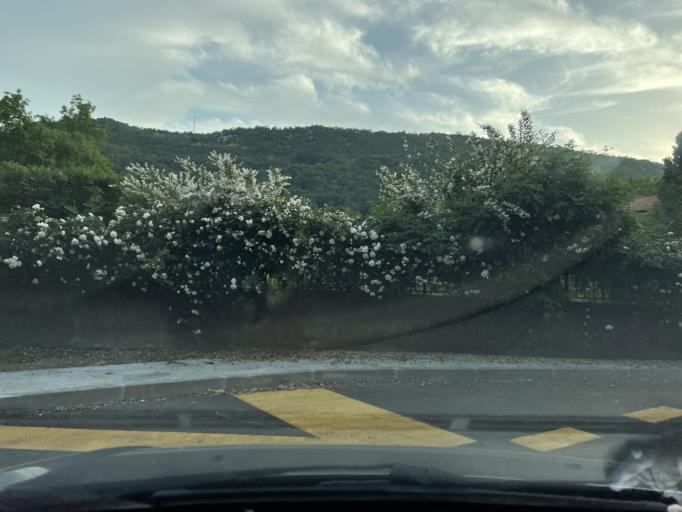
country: HR
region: Primorsko-Goranska
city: Marcelji
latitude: 45.3960
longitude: 14.4257
